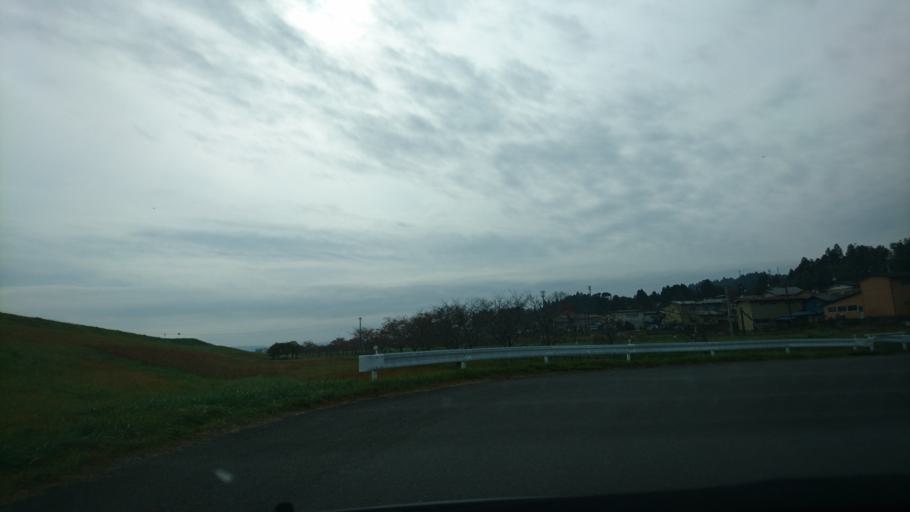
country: JP
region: Iwate
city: Ichinoseki
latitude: 38.9569
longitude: 141.1307
